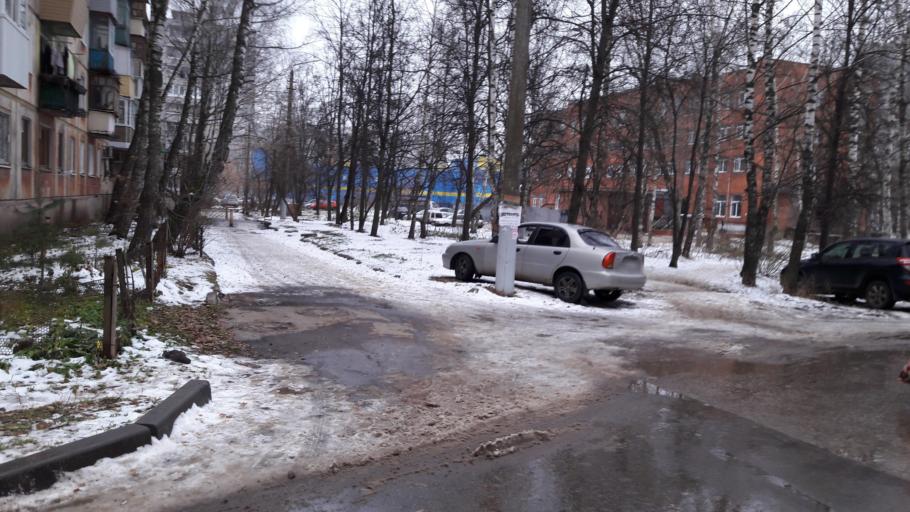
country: RU
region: Tula
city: Tula
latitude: 54.1939
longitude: 37.6871
